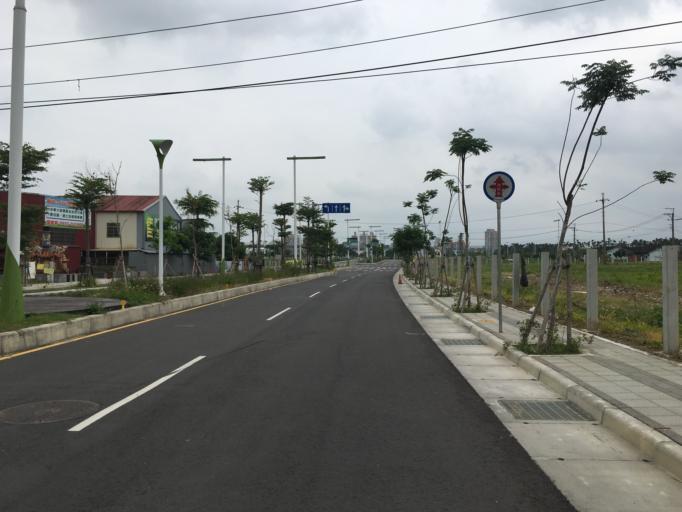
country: TW
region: Taiwan
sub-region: Taichung City
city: Taichung
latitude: 24.1914
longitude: 120.7071
